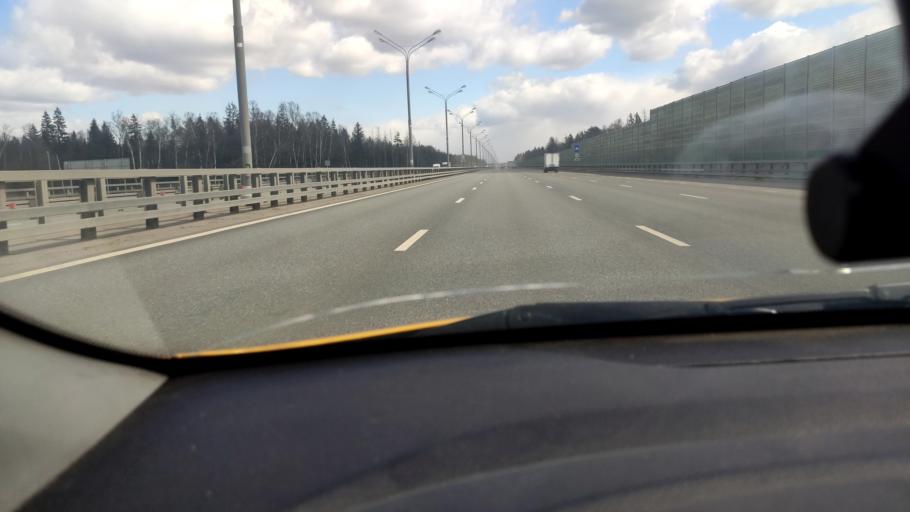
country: RU
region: Moskovskaya
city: Krasnoznamensk
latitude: 55.6056
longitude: 37.0288
